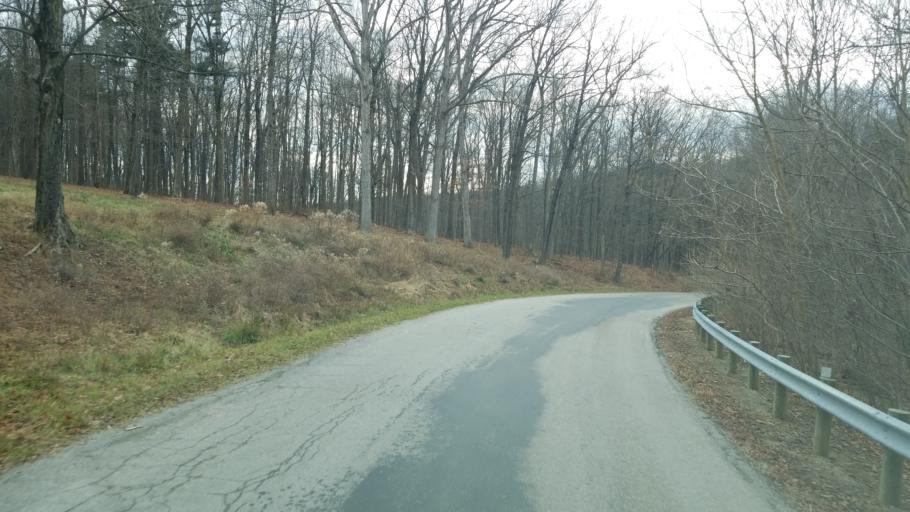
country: US
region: Ohio
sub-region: Highland County
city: Greenfield
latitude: 39.1769
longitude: -83.2690
